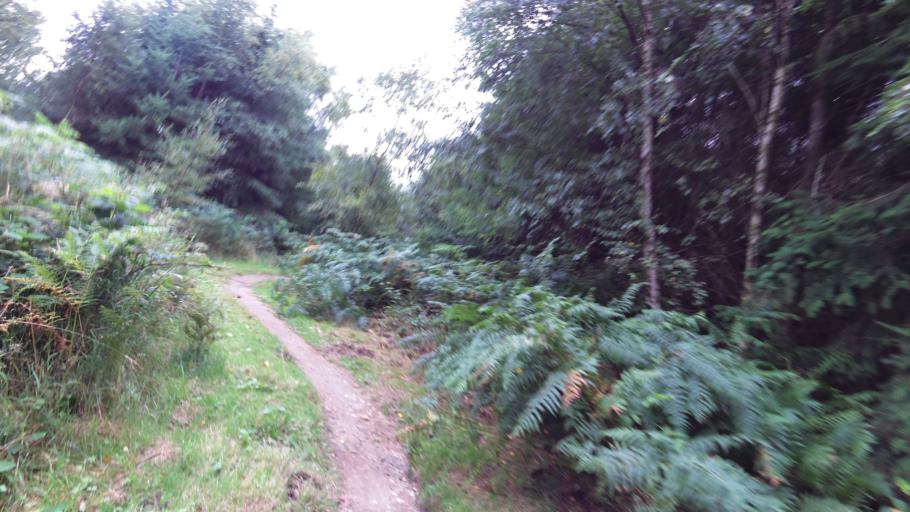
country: GB
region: England
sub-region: North Yorkshire
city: Thornton Dale
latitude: 54.2888
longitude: -0.6845
